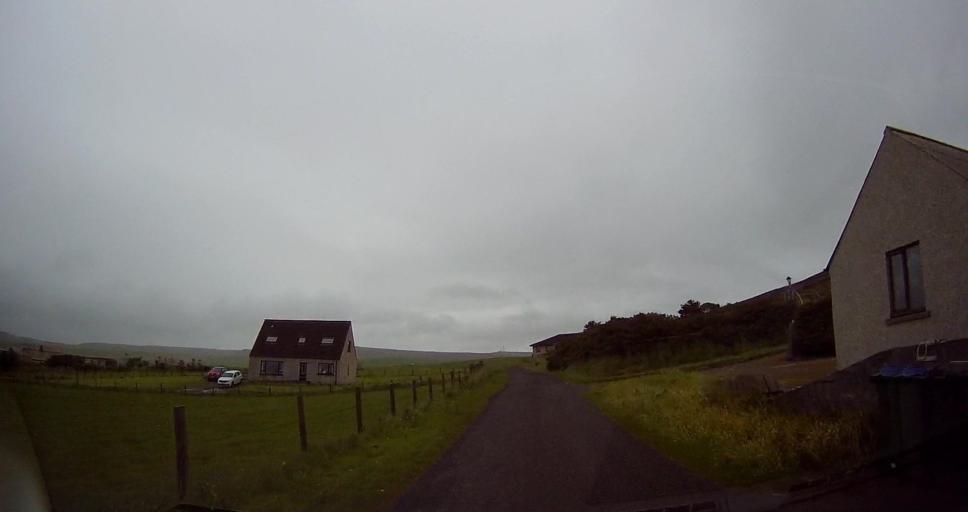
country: GB
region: Scotland
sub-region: Orkney Islands
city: Stromness
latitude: 58.9765
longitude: -3.1597
